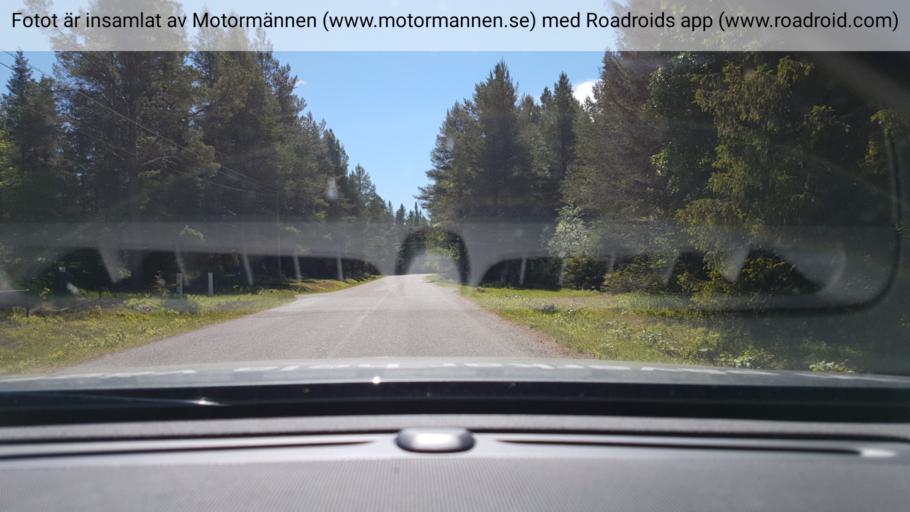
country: SE
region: Vaesterbotten
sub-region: Skelleftea Kommun
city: Skelleftehamn
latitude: 64.4697
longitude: 21.5844
